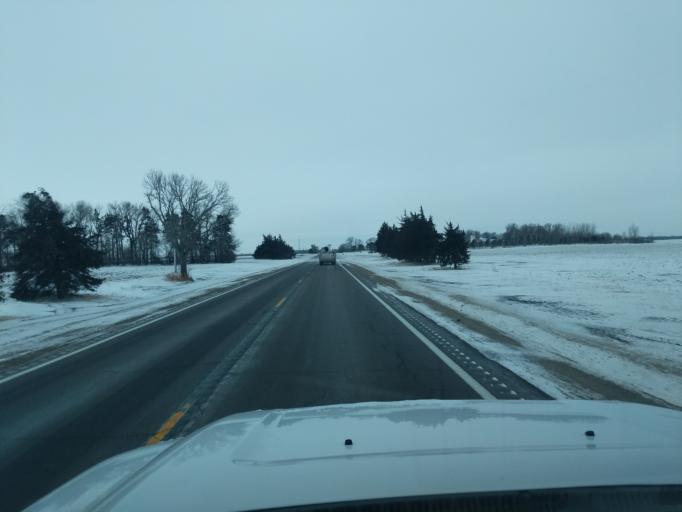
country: US
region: Minnesota
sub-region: Redwood County
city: Redwood Falls
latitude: 44.5910
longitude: -94.9945
